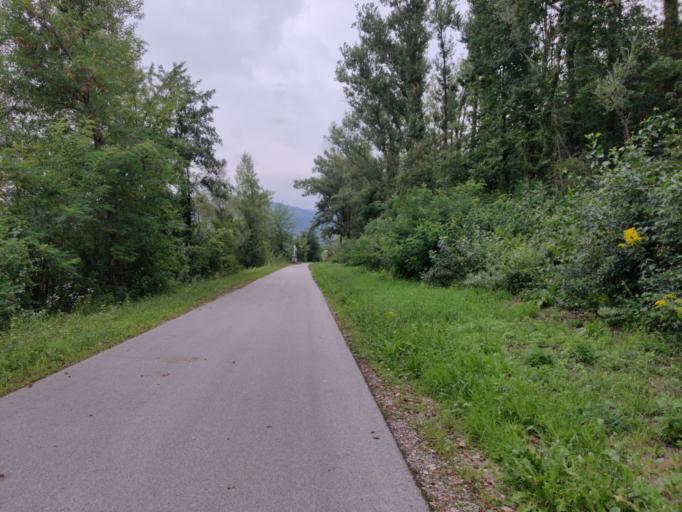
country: AT
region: Lower Austria
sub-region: Politischer Bezirk Melk
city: Ybbs an der Donau
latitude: 48.1888
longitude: 15.1154
